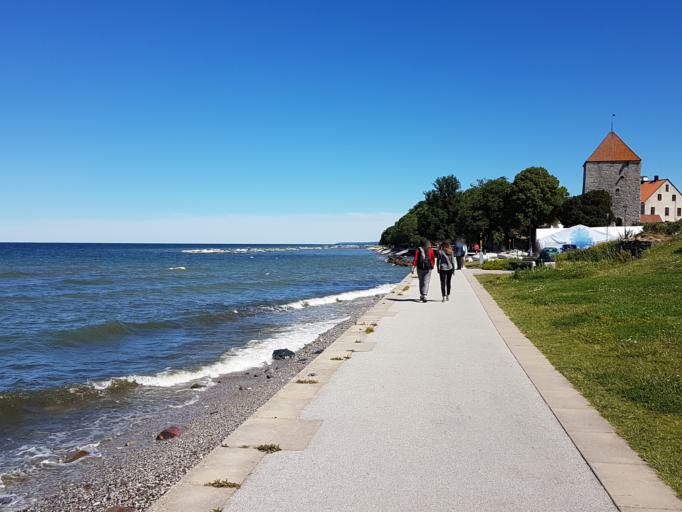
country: SE
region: Gotland
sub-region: Gotland
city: Visby
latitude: 57.6414
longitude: 18.2894
